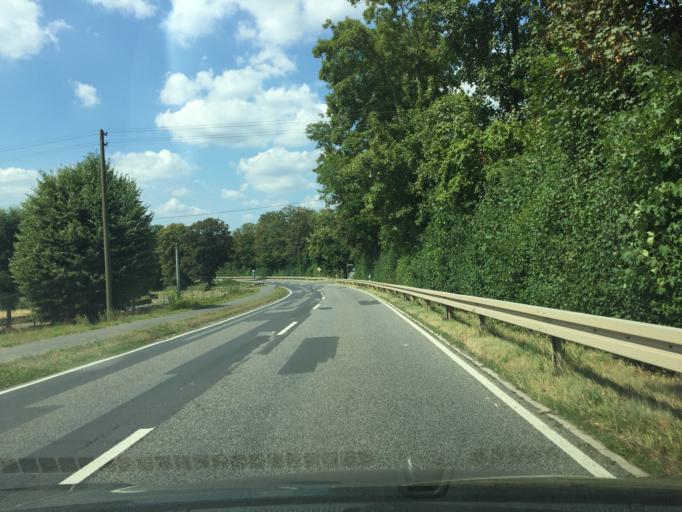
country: DE
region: Hesse
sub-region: Regierungsbezirk Giessen
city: Elz
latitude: 50.4674
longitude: 8.0460
